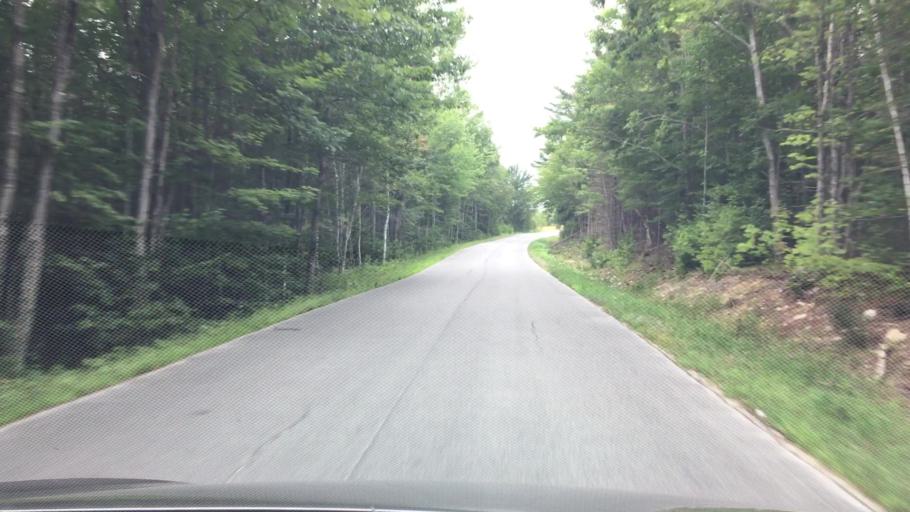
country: US
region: Maine
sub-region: Waldo County
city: Stockton Springs
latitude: 44.5205
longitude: -68.8795
